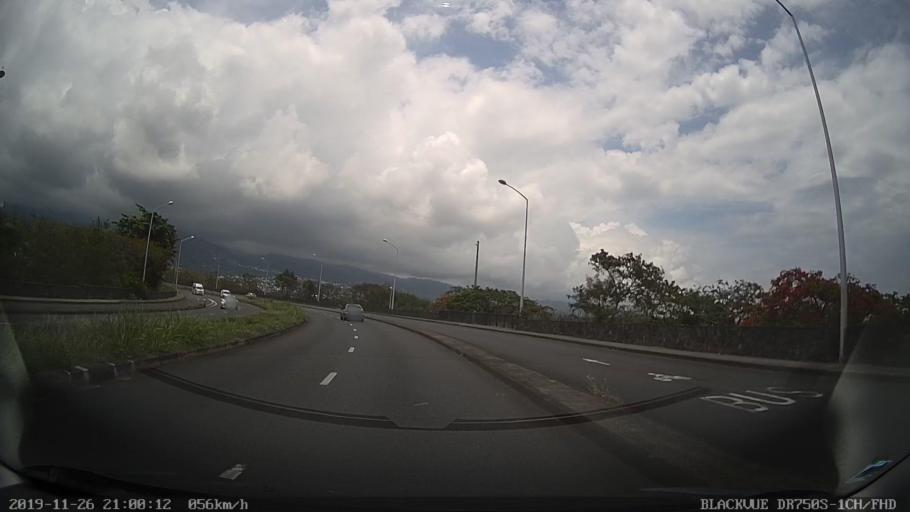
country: RE
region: Reunion
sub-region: Reunion
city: Sainte-Marie
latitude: -20.8980
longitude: 55.5080
